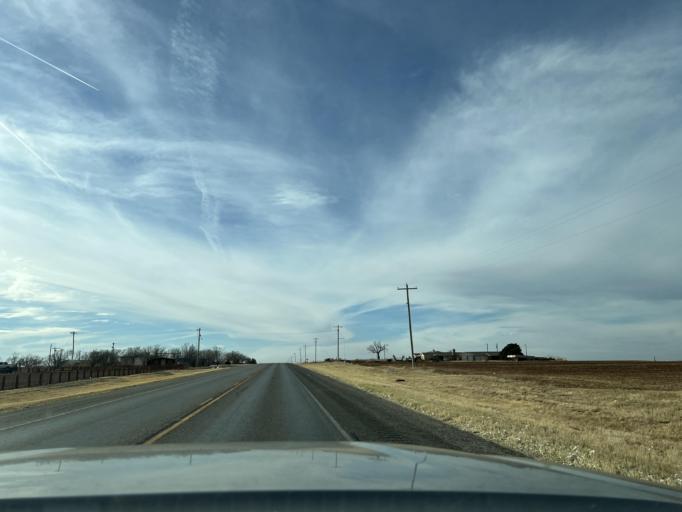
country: US
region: Texas
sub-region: Jones County
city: Anson
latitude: 32.7518
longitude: -99.9154
